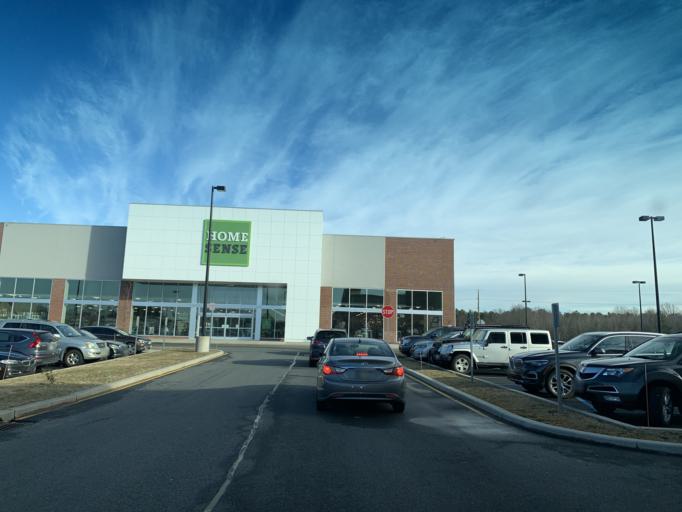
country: US
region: Delaware
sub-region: New Castle County
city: Bear
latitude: 39.6702
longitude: -75.6488
